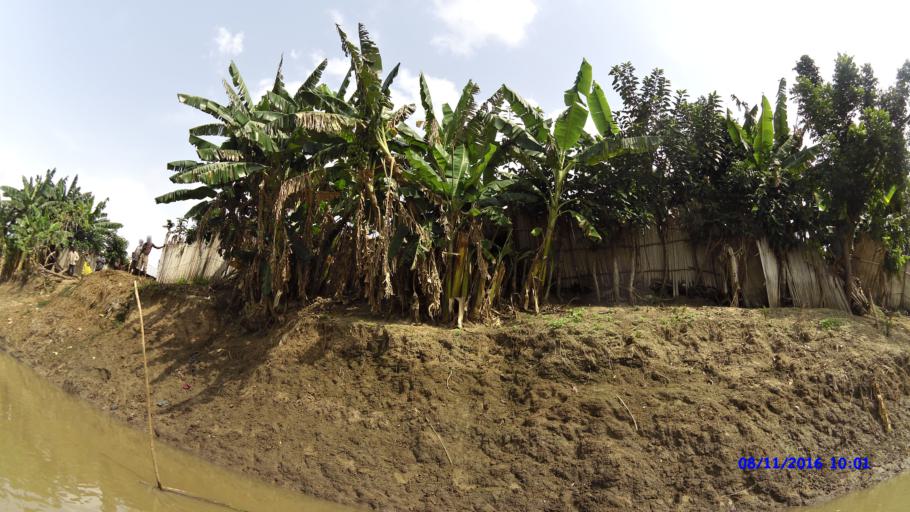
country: BJ
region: Mono
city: Come
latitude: 6.4409
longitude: 1.7623
